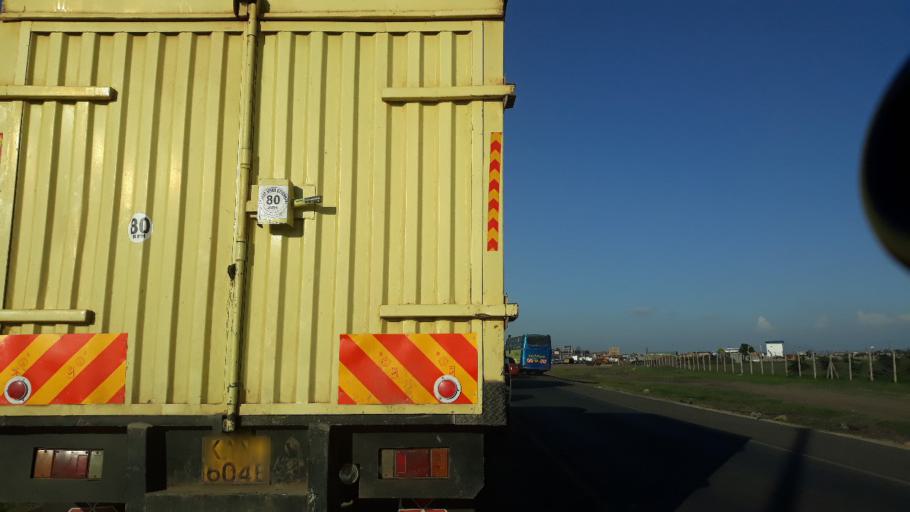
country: KE
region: Nairobi Area
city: Pumwani
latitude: -1.2941
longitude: 36.9430
